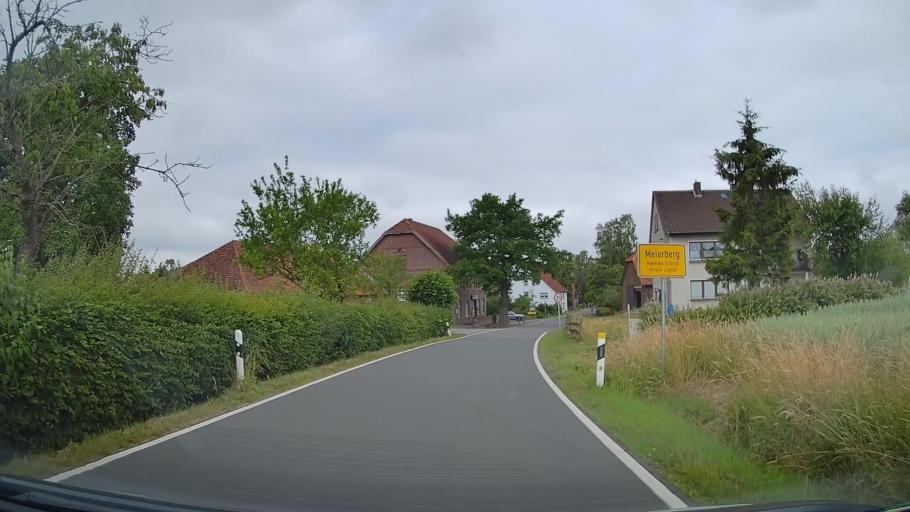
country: DE
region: Lower Saxony
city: Rinteln
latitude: 52.1004
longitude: 9.1227
